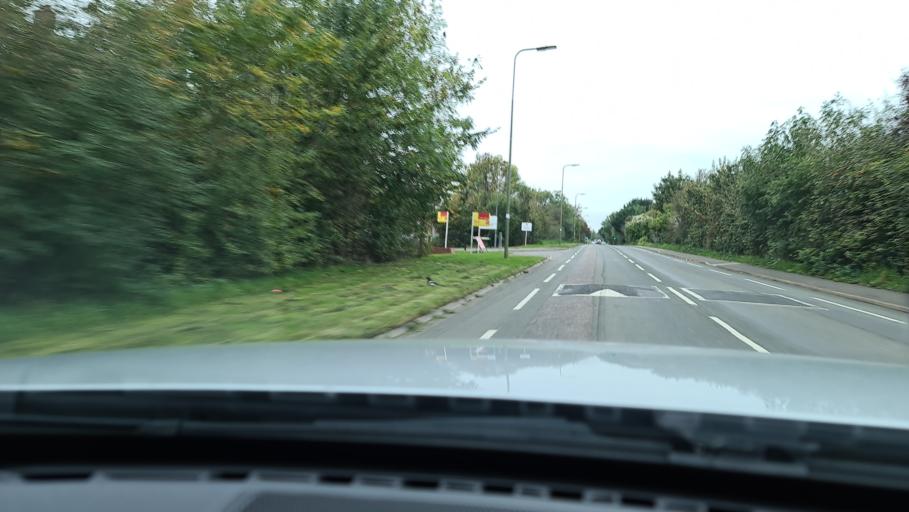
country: GB
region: England
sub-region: Oxfordshire
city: Bicester
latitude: 51.8969
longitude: -1.1659
